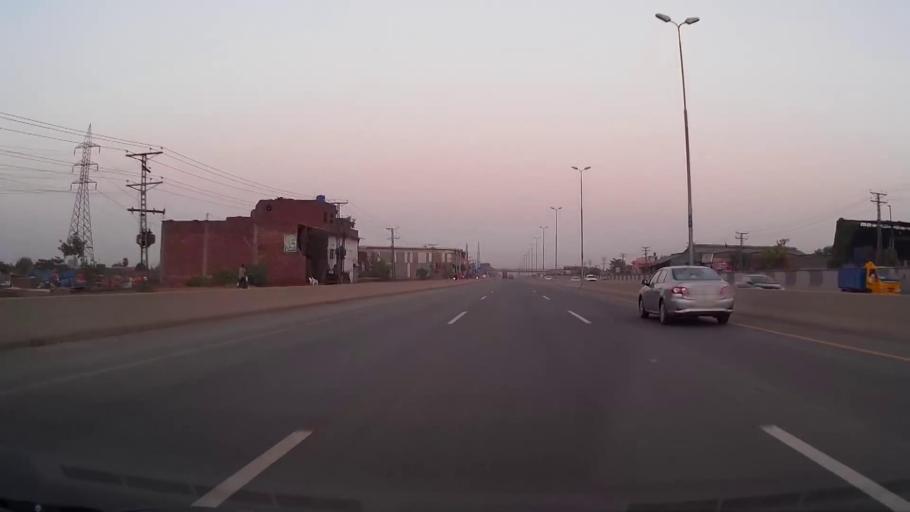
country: PK
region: Punjab
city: Lahore
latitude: 31.6092
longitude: 74.3406
